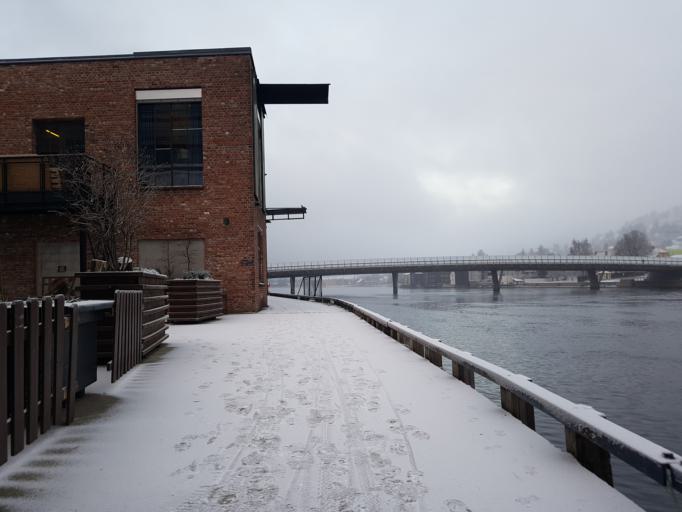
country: NO
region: Buskerud
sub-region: Drammen
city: Drammen
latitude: 59.7444
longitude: 10.1933
